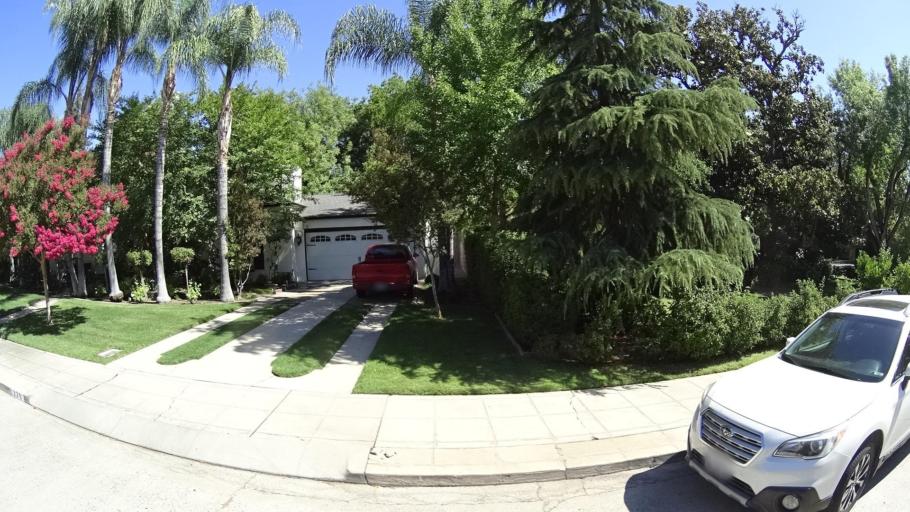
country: US
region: California
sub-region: Fresno County
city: Fresno
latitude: 36.7731
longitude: -119.8089
